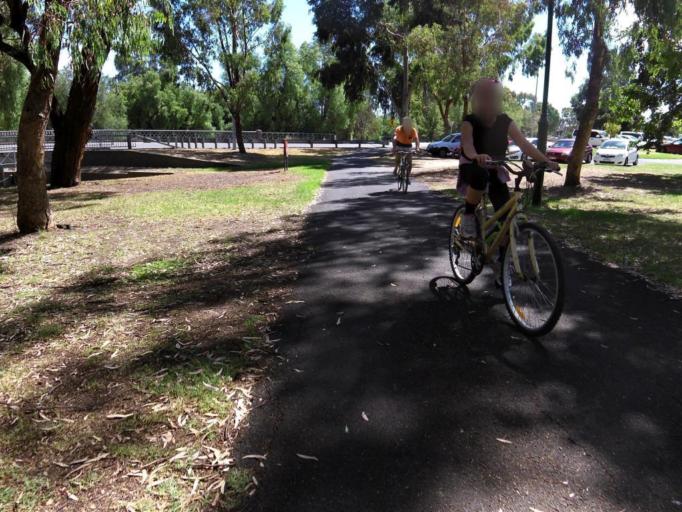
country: AU
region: Victoria
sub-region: Greater Bendigo
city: Bendigo
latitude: -36.7440
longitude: 144.2920
